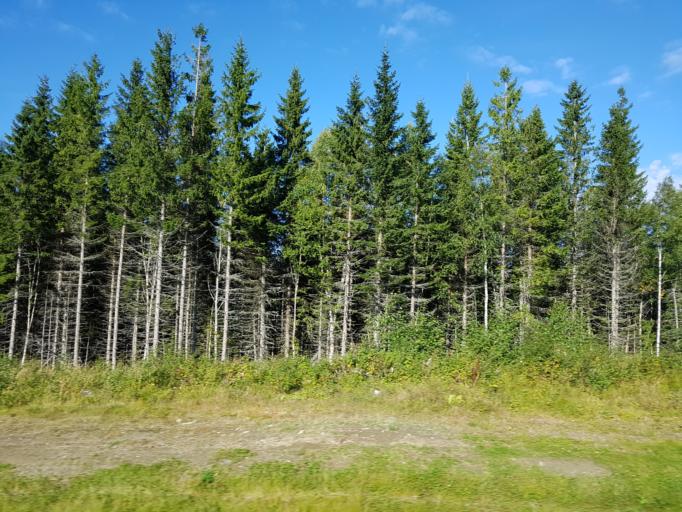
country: NO
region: Sor-Trondelag
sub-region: Trondheim
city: Trondheim
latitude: 63.6234
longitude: 10.2439
